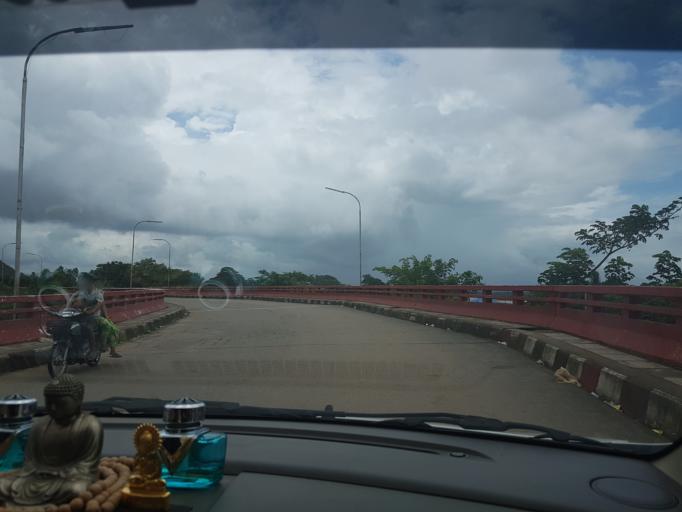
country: MM
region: Bago
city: Nyaunglebin
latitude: 17.9140
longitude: 96.8476
